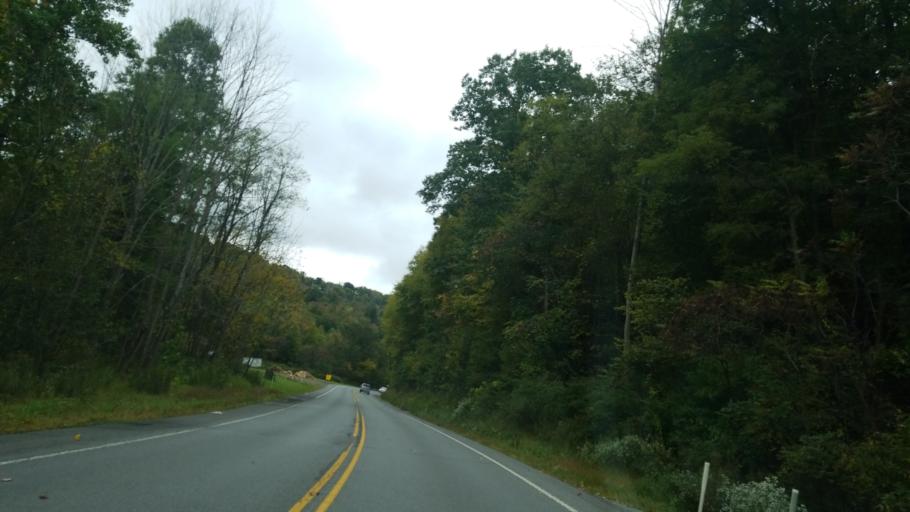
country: US
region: Pennsylvania
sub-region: Clearfield County
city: Curwensville
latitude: 40.9741
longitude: -78.5527
